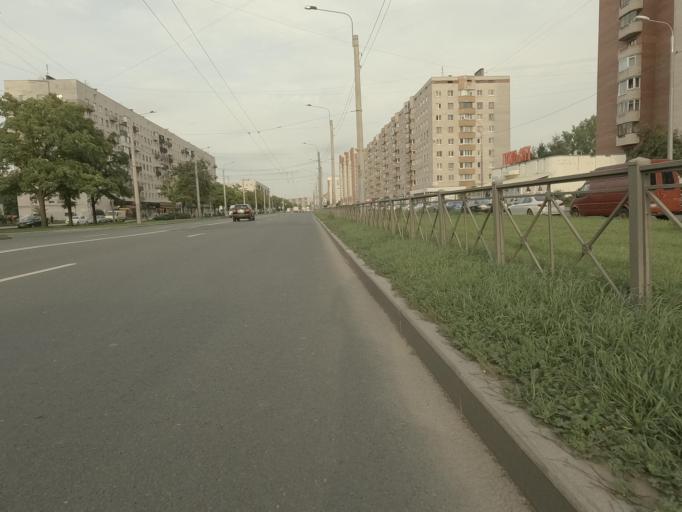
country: RU
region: St.-Petersburg
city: Uritsk
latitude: 59.8330
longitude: 30.1986
